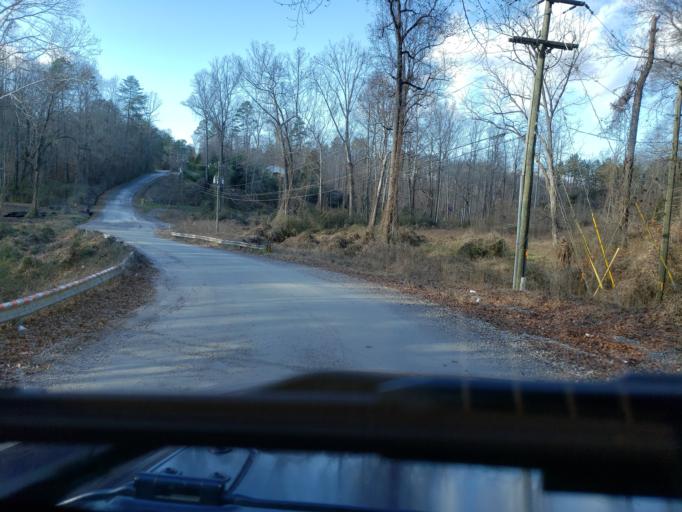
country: US
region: North Carolina
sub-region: Cleveland County
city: Kings Mountain
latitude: 35.1577
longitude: -81.3371
